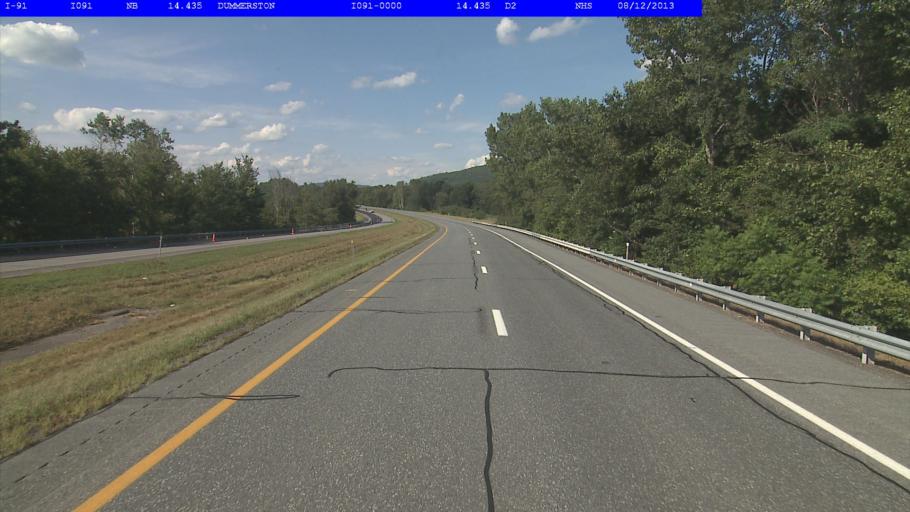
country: US
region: New Hampshire
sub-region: Cheshire County
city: Chesterfield
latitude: 42.9183
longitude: -72.5278
